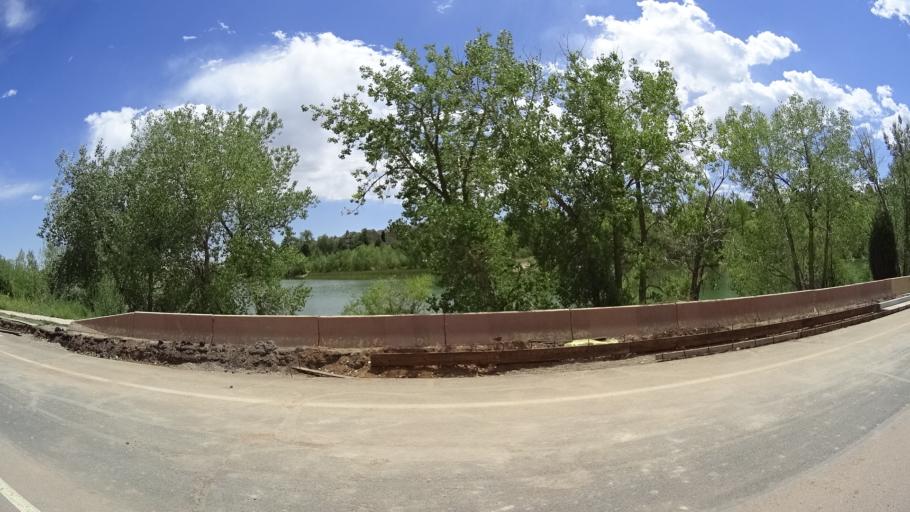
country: US
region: Colorado
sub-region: El Paso County
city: Stratmoor
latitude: 38.7858
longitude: -104.8104
